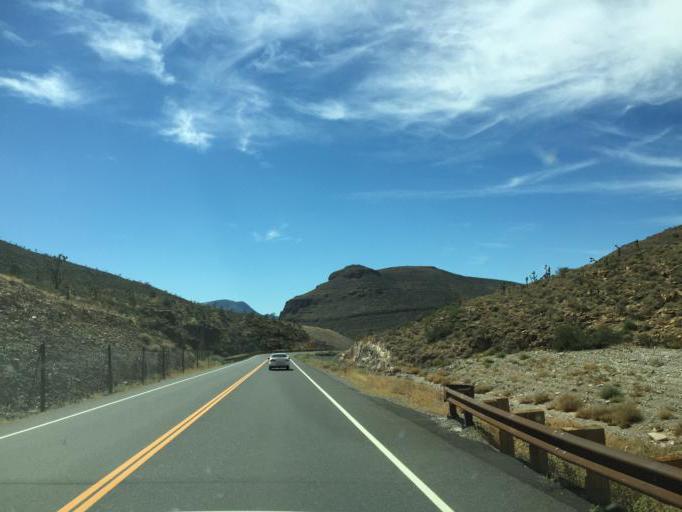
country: US
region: Arizona
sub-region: Mohave County
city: Meadview
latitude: 35.9015
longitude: -113.9379
